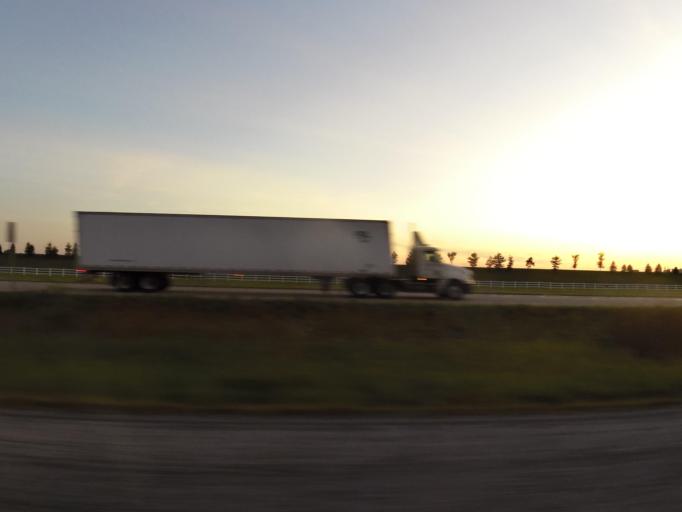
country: US
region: Indiana
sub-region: Decatur County
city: Greensburg
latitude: 39.3676
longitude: -85.5247
